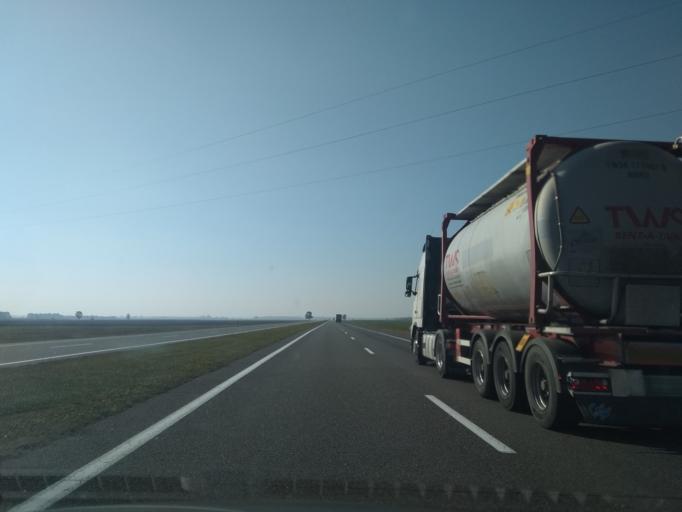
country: BY
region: Brest
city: Byaroza
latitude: 52.4411
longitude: 24.8830
